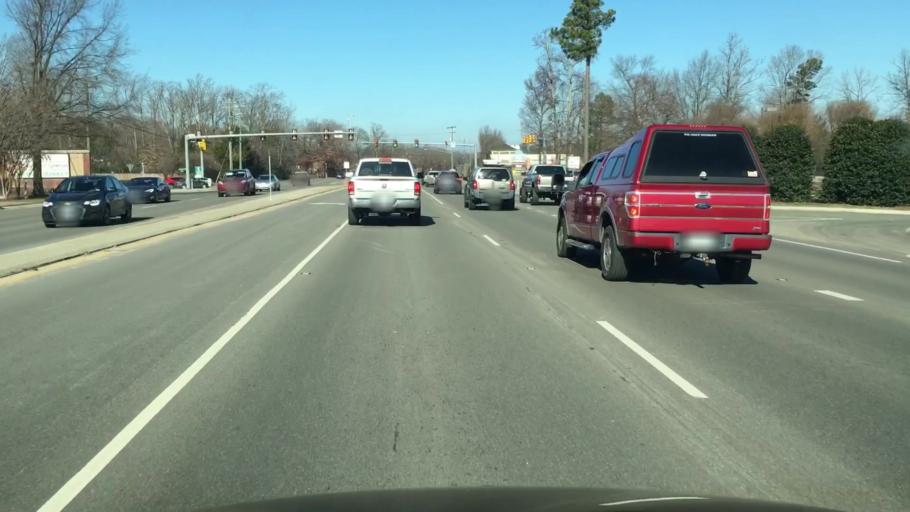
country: US
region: Virginia
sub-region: Chesterfield County
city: Bon Air
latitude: 37.5101
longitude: -77.6136
